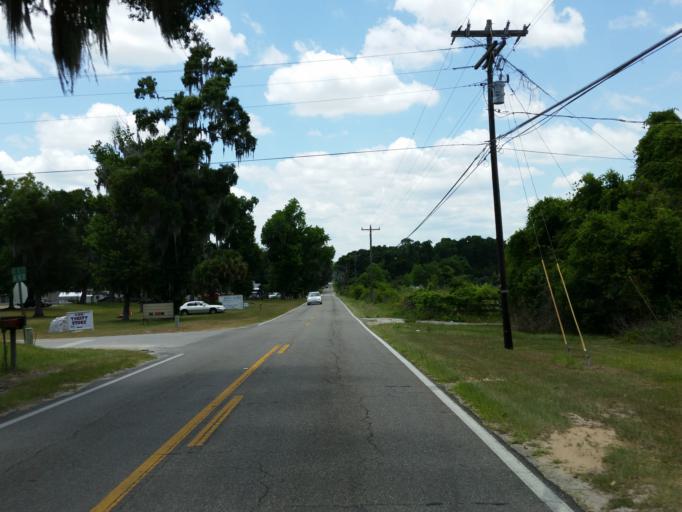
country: US
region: Florida
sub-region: Marion County
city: Belleview
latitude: 29.0114
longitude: -82.0617
